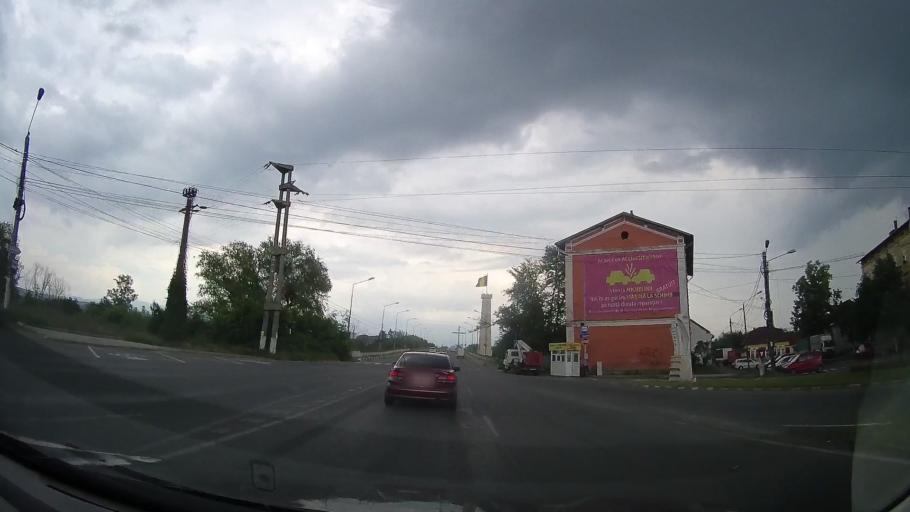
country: RO
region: Caras-Severin
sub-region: Municipiul Caransebes
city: Caransebes
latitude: 45.4158
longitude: 22.1992
